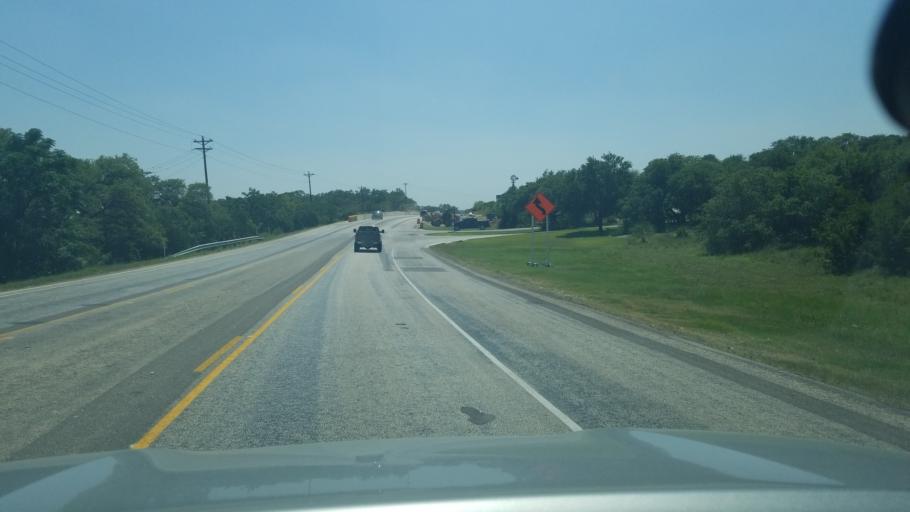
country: US
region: Texas
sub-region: Bexar County
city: Fair Oaks Ranch
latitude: 29.8216
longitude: -98.5826
